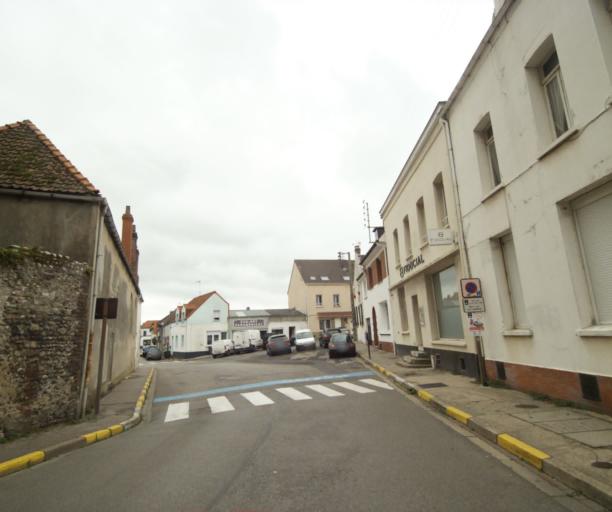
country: FR
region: Nord-Pas-de-Calais
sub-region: Departement du Pas-de-Calais
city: Etaples
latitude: 50.5155
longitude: 1.6412
